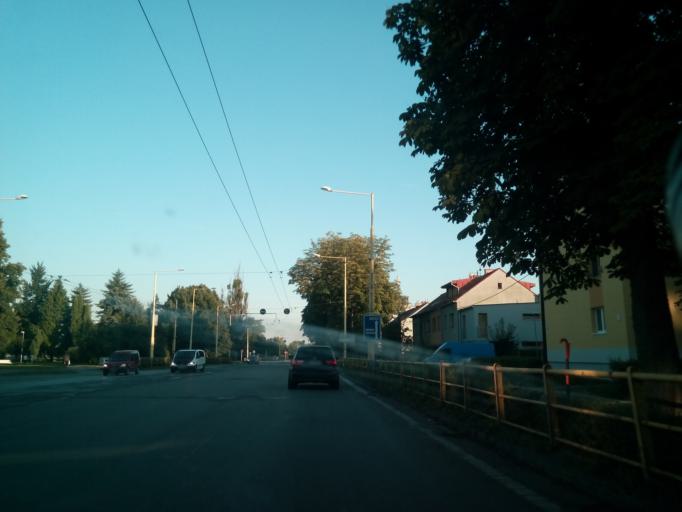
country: SK
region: Presovsky
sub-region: Okres Presov
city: Presov
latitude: 48.9957
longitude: 21.2291
